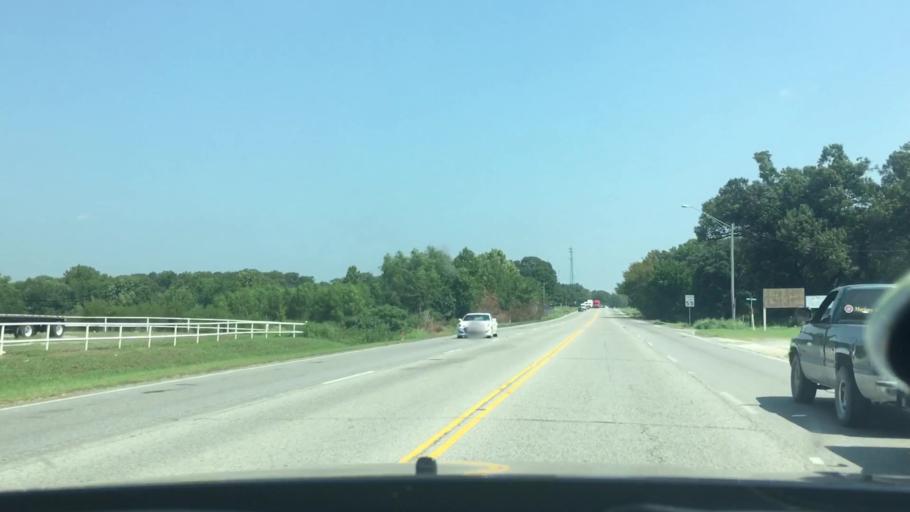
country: US
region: Oklahoma
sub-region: Atoka County
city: Atoka
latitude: 34.3215
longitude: -96.1665
